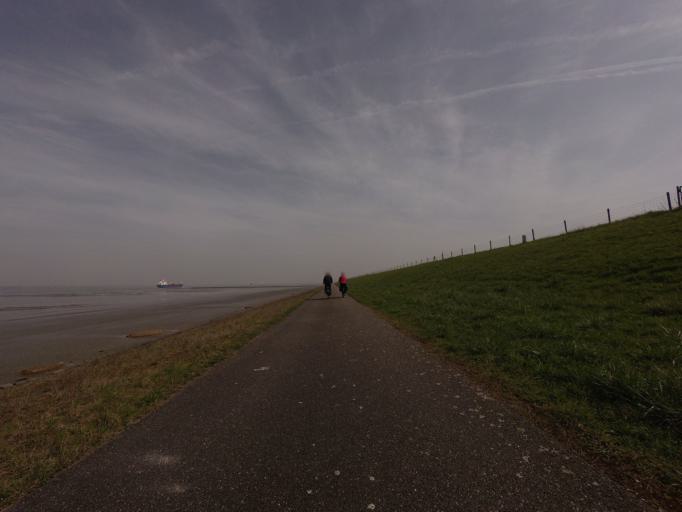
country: NL
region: Zeeland
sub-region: Gemeente Hulst
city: Hulst
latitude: 51.3649
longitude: 4.0680
